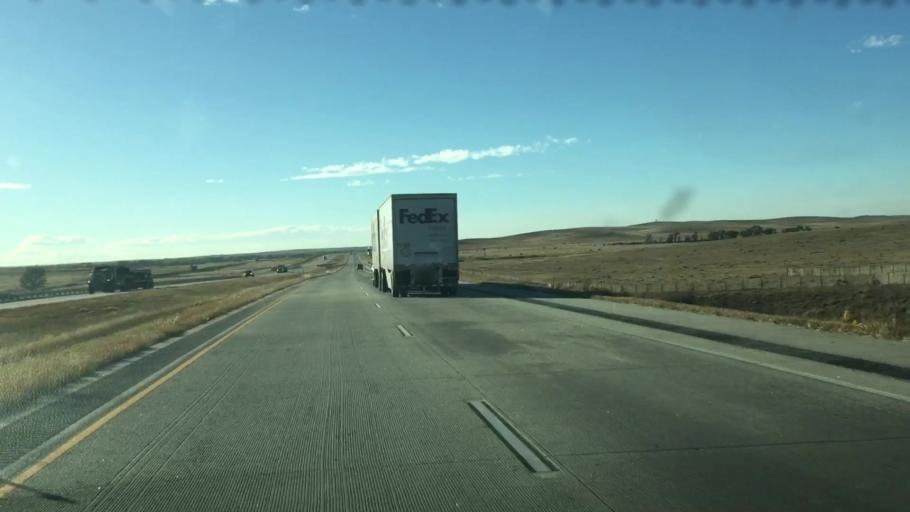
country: US
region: Colorado
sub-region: Lincoln County
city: Limon
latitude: 39.2823
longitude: -103.7732
